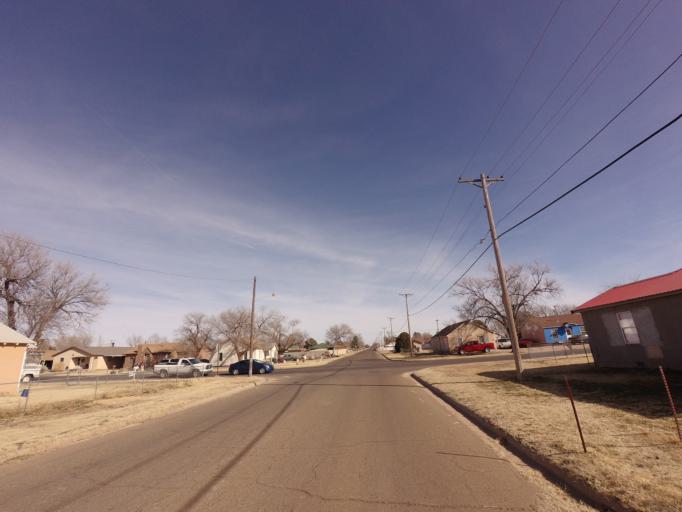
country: US
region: New Mexico
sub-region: Curry County
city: Clovis
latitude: 34.4068
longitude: -103.2209
